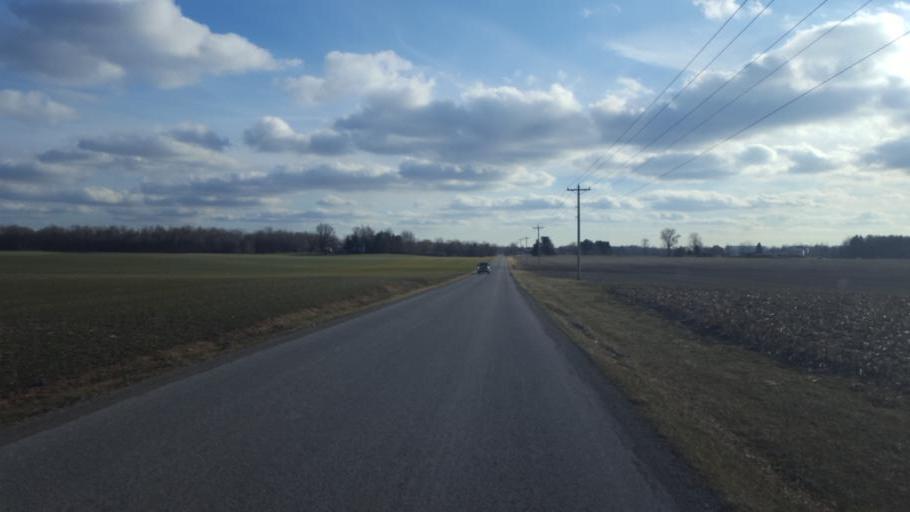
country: US
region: Ohio
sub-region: Morrow County
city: Mount Gilead
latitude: 40.5936
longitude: -82.7288
